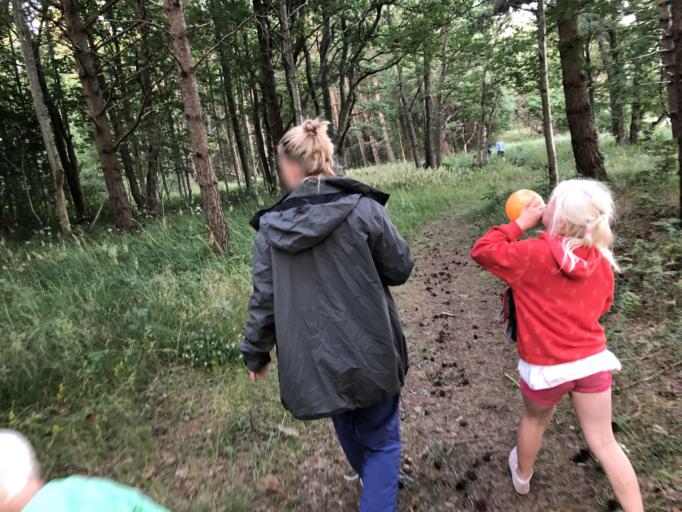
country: EE
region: Hiiumaa
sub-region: Kaerdla linn
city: Kardla
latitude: 58.8840
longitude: 22.2510
